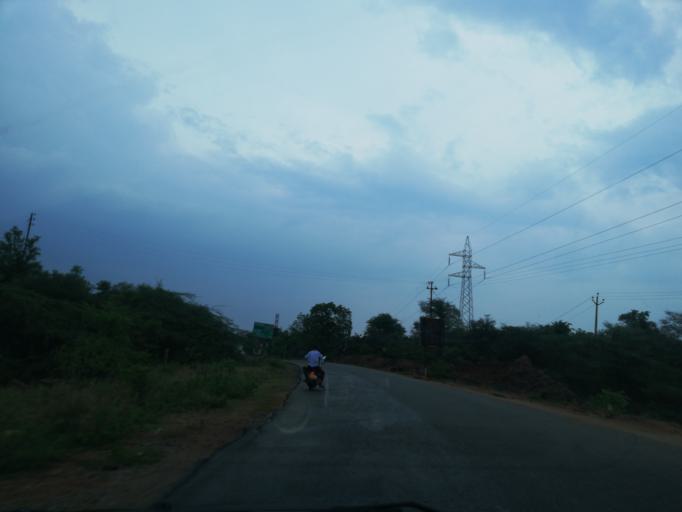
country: IN
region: Andhra Pradesh
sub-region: Guntur
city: Macherla
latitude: 16.6621
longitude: 79.2865
